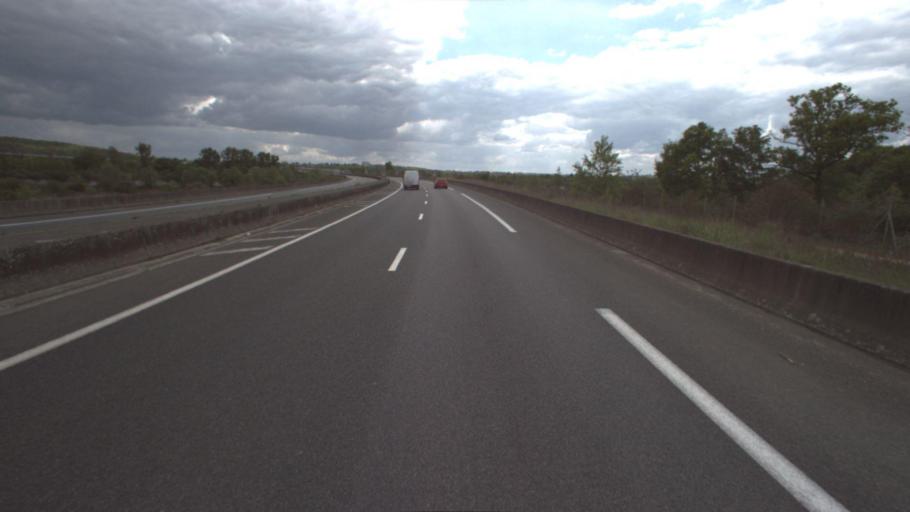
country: FR
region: Ile-de-France
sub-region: Departement de Seine-et-Marne
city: Mareuil-les-Meaux
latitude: 48.9254
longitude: 2.8448
